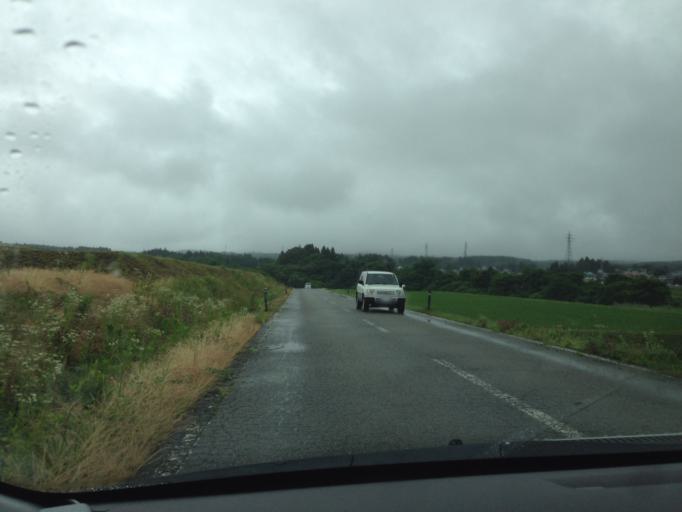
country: JP
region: Fukushima
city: Inawashiro
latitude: 37.5656
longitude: 139.9934
